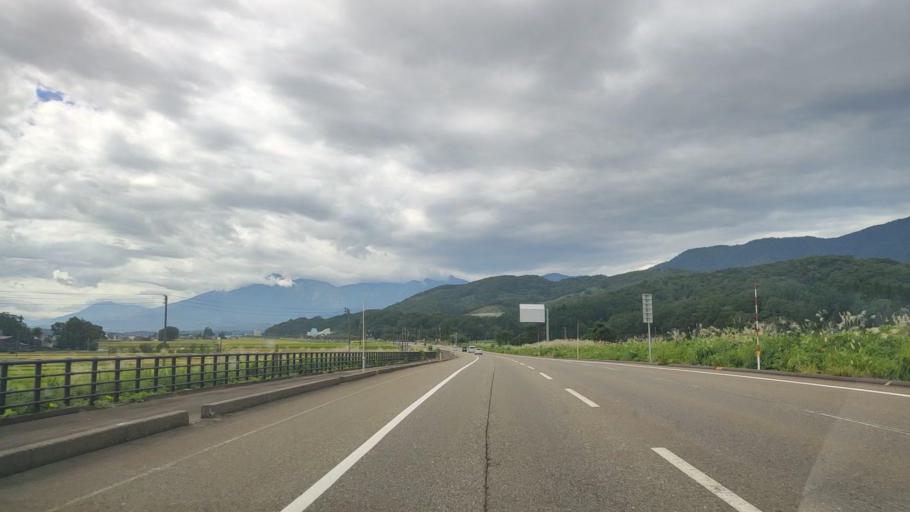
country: JP
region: Niigata
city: Arai
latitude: 37.0485
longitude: 138.2437
